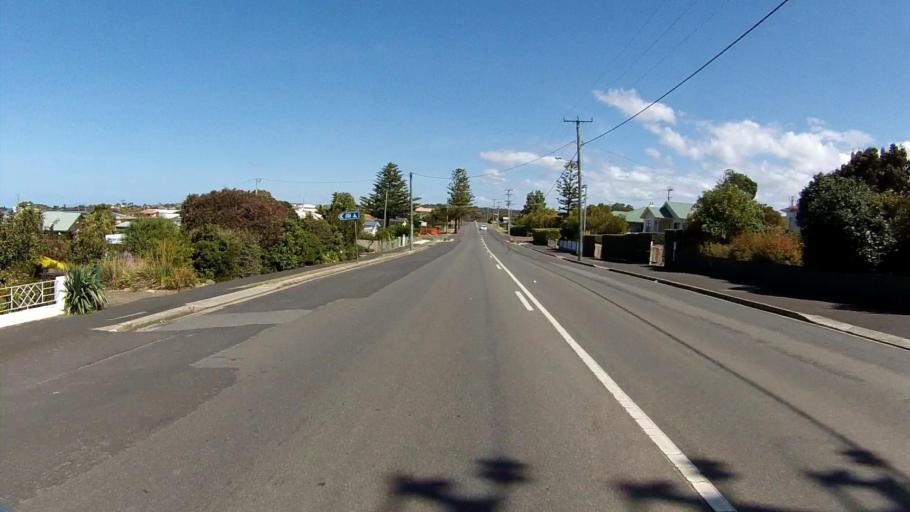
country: AU
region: Tasmania
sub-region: Break O'Day
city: St Helens
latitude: -42.1254
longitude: 148.0771
